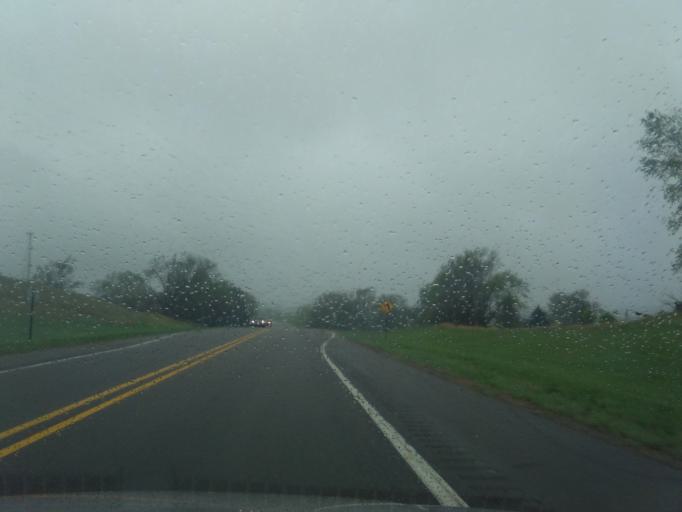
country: US
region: Nebraska
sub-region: Madison County
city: Norfolk
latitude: 42.1053
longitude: -97.3039
